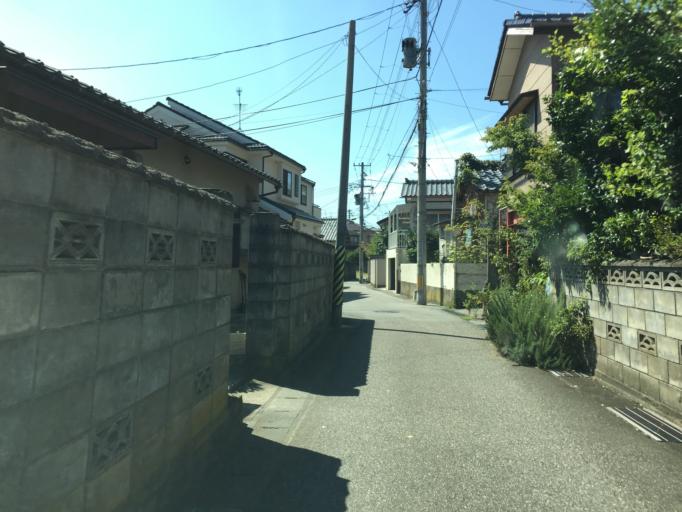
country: JP
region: Niigata
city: Niigata-shi
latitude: 37.9034
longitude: 138.9999
